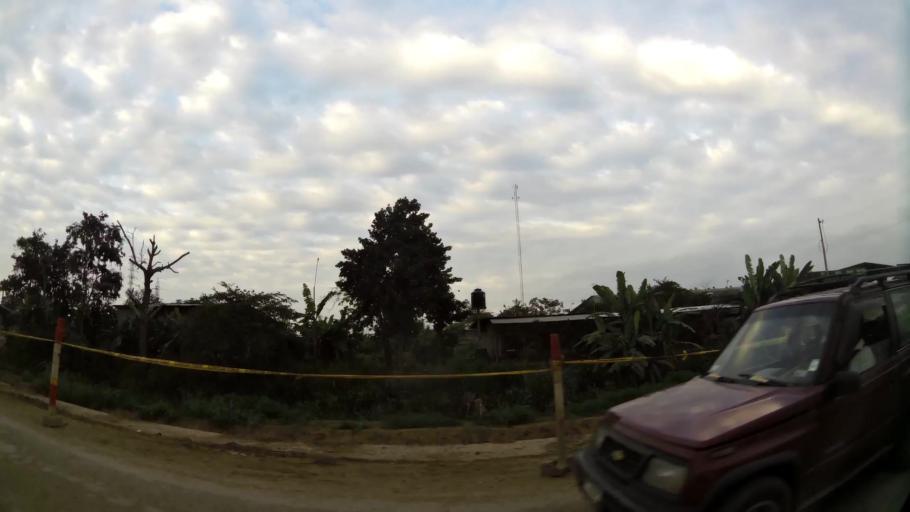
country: EC
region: El Oro
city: Machala
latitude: -3.2717
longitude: -79.9318
